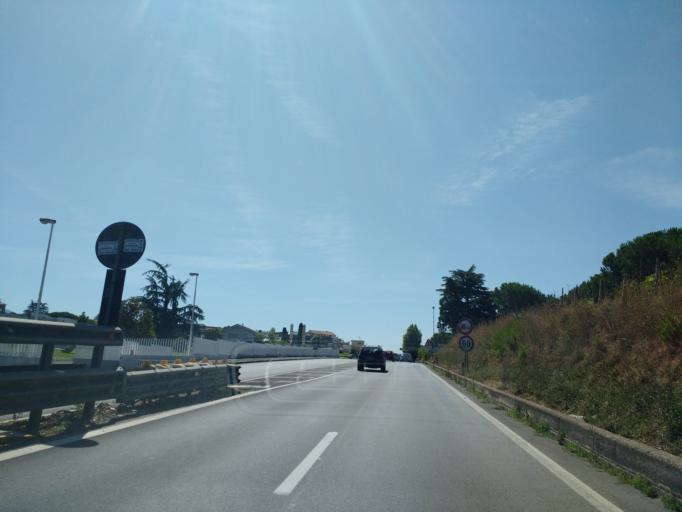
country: IT
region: Latium
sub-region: Citta metropolitana di Roma Capitale
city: Marino
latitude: 41.7688
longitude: 12.6146
